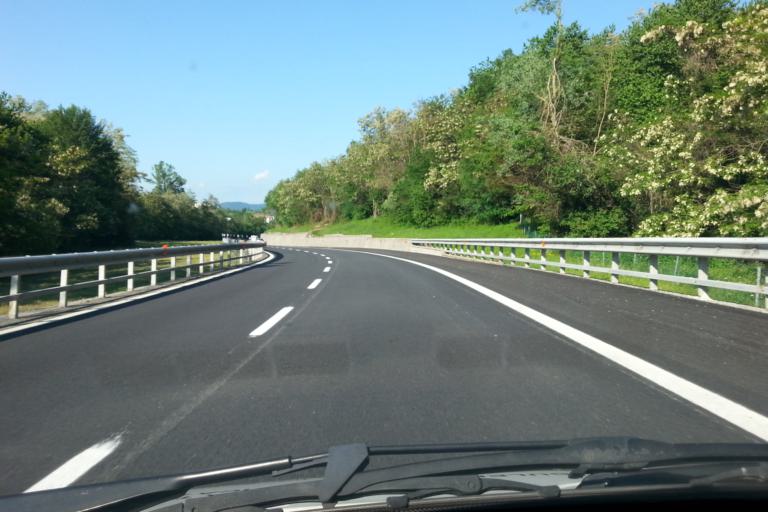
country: IT
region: Liguria
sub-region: Provincia di Savona
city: Cosseria
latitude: 44.3584
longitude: 8.2333
